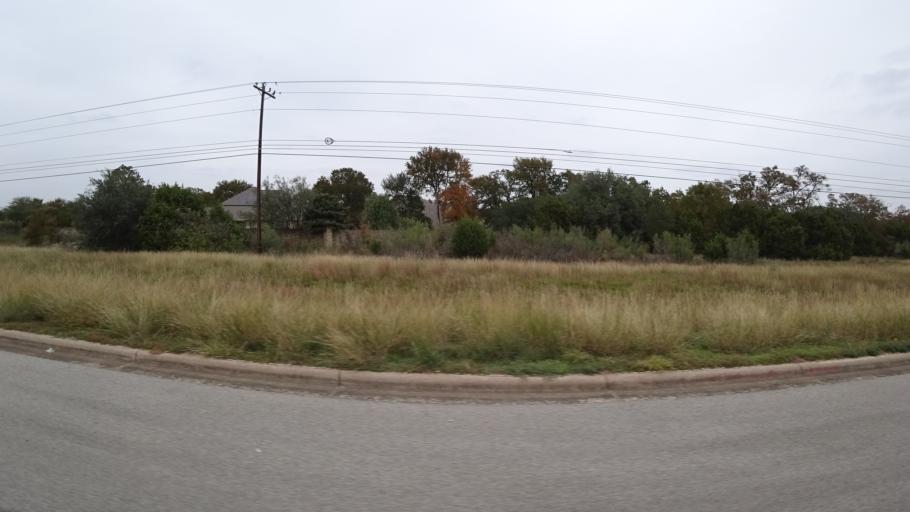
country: US
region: Texas
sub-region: Travis County
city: Shady Hollow
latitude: 30.1905
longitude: -97.9192
